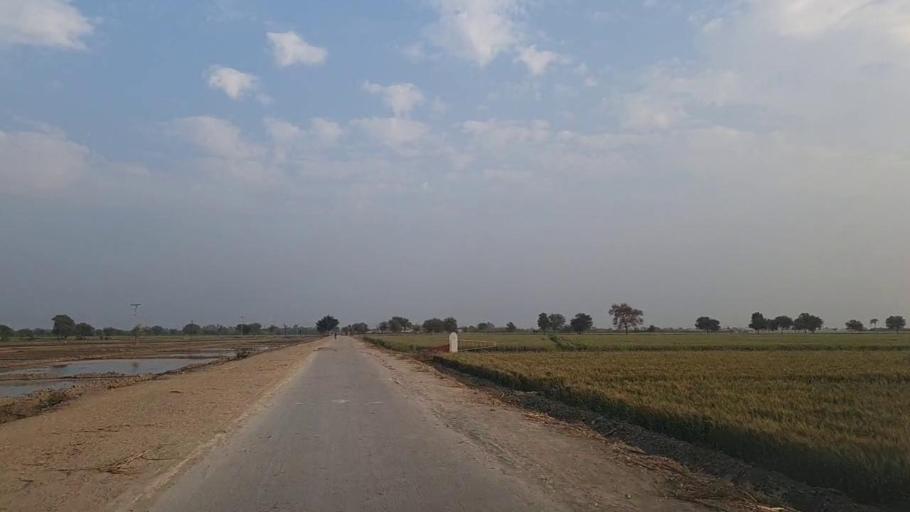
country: PK
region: Sindh
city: Samaro
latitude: 25.2951
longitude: 69.2272
